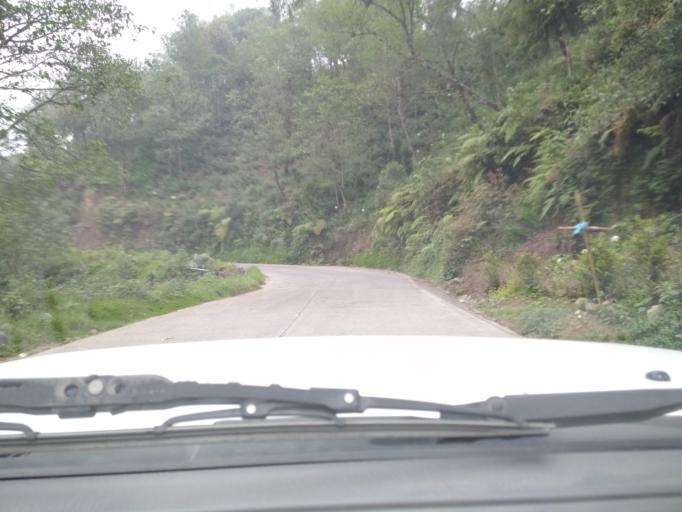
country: MX
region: Veracruz
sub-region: La Perla
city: Metlac Hernandez (Metlac Primero)
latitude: 18.9720
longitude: -97.1551
